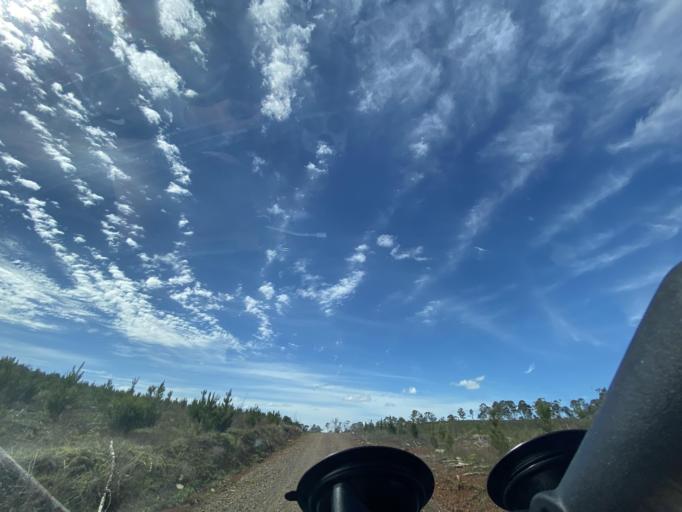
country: AU
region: Victoria
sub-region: Mansfield
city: Mansfield
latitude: -36.8291
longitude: 146.1024
